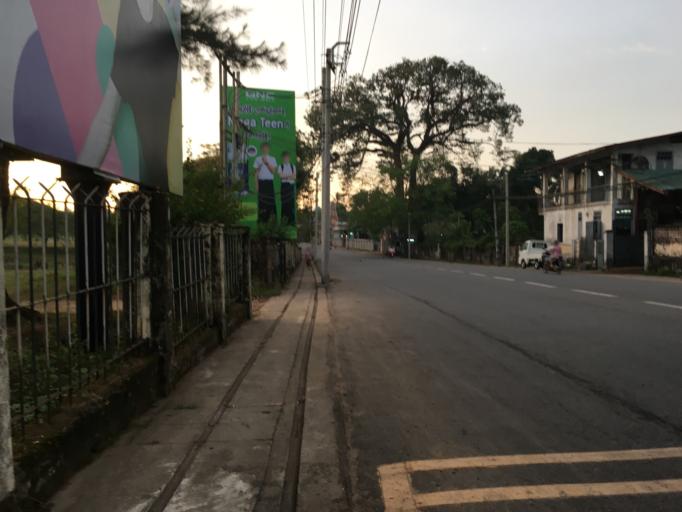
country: MM
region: Mon
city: Mawlamyine
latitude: 16.4680
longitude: 97.6265
